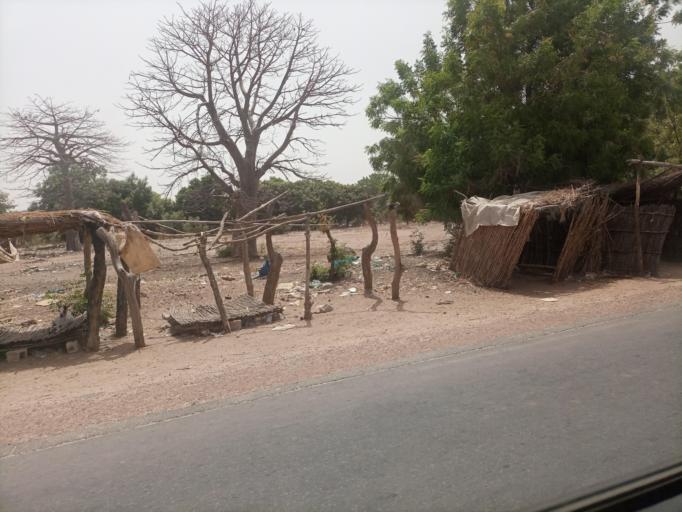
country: SN
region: Fatick
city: Sokone
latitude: 13.7249
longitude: -16.4239
